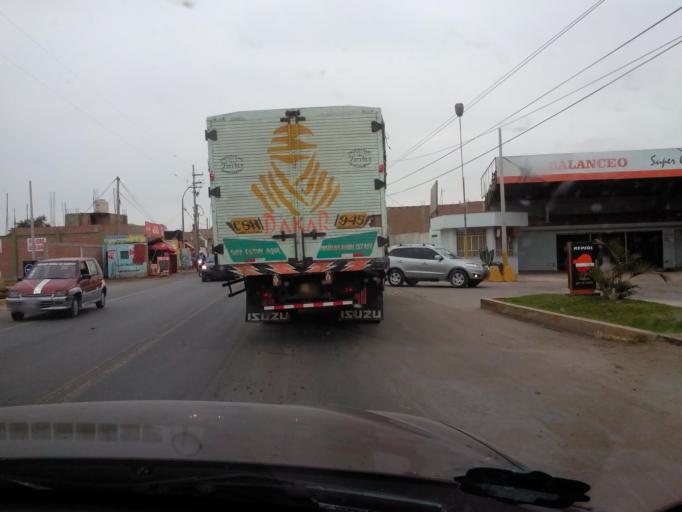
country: PE
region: Ica
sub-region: Provincia de Chincha
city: Chincha Alta
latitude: -13.4319
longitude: -76.1343
